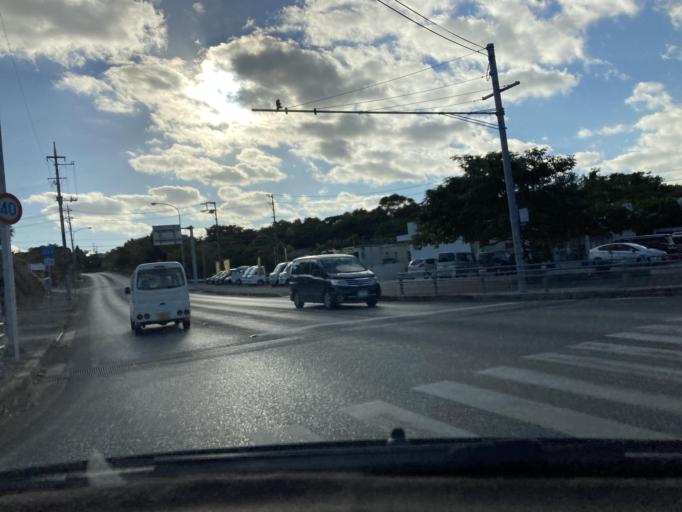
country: JP
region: Okinawa
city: Gushikawa
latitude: 26.3646
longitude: 127.8540
